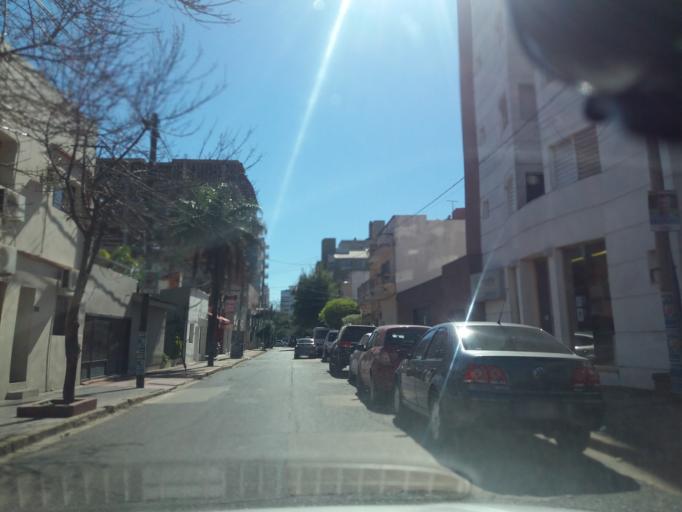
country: AR
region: Corrientes
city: Corrientes
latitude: -27.4681
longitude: -58.8430
